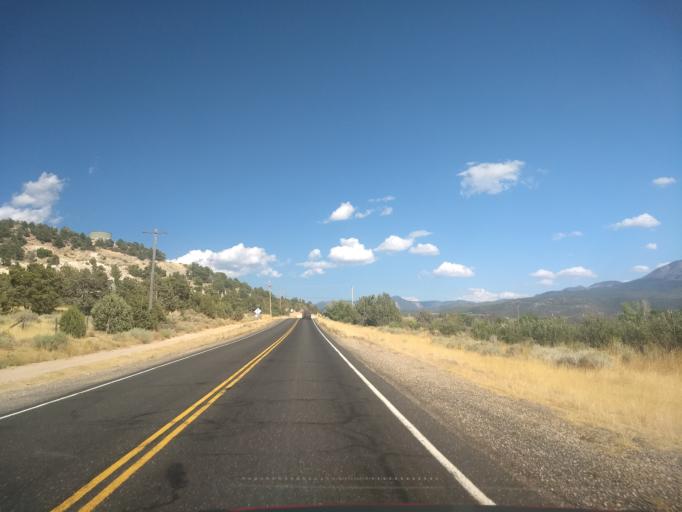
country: US
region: Utah
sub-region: Washington County
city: Enterprise
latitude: 37.4170
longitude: -113.6285
